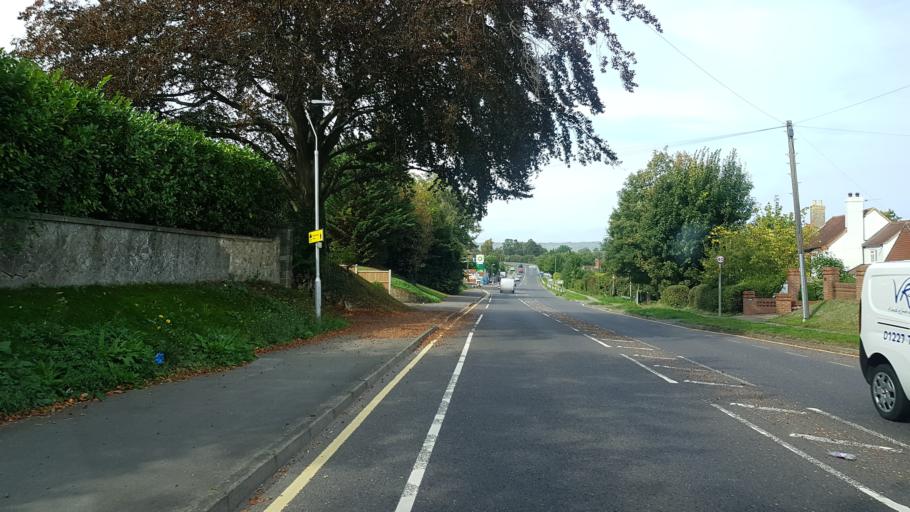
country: GB
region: England
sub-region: Kent
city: West Malling
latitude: 51.2994
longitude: 0.4083
